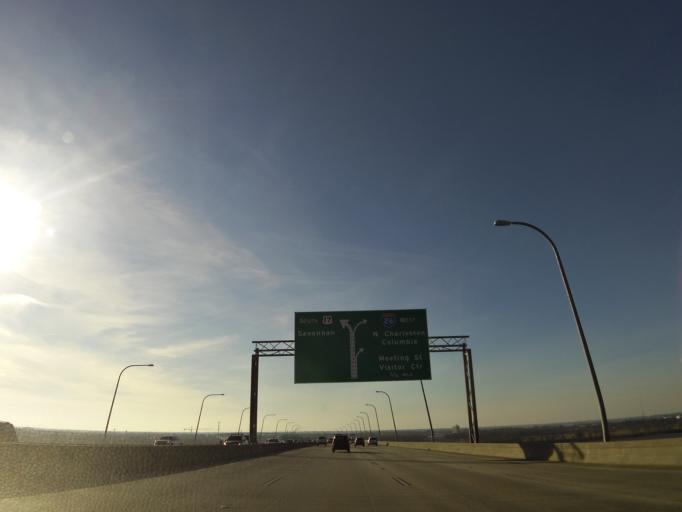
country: US
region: South Carolina
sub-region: Charleston County
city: Charleston
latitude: 32.8045
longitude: -79.9270
